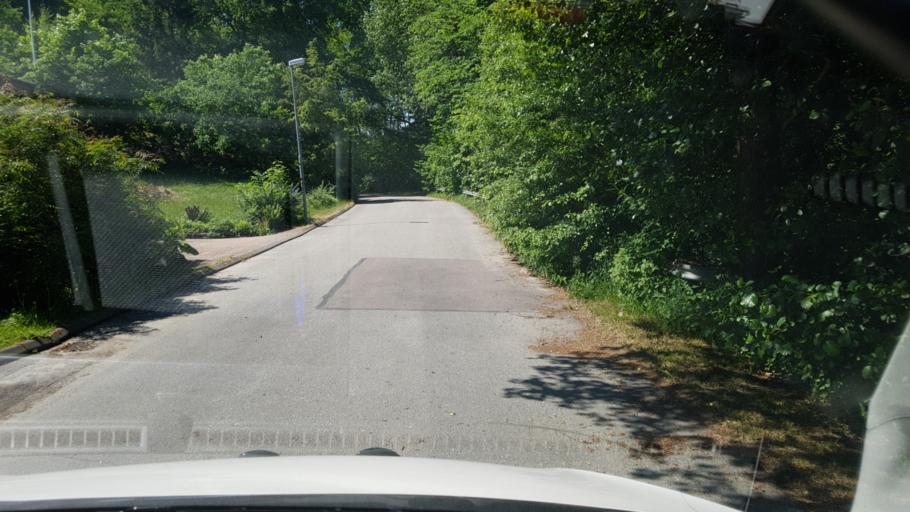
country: SE
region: Vaestra Goetaland
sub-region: Lerums Kommun
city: Stenkullen
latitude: 57.8050
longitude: 12.3556
